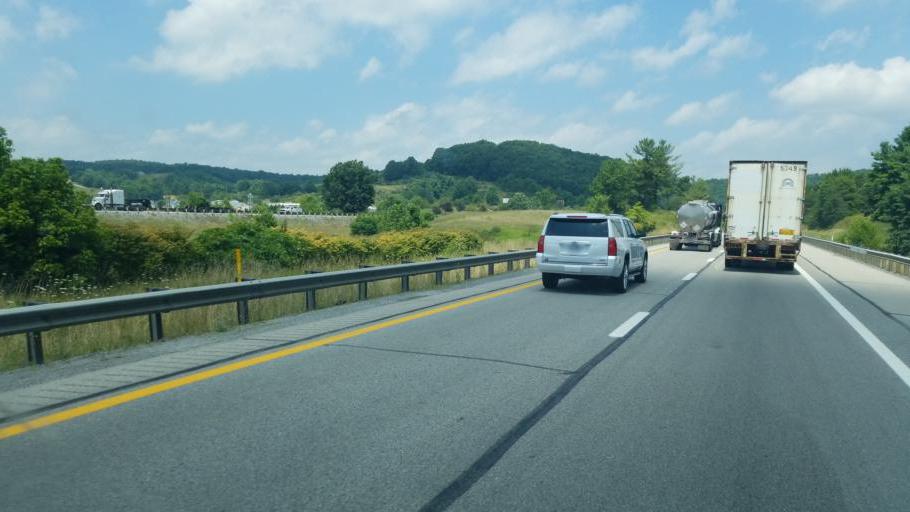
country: US
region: West Virginia
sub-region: Mercer County
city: Athens
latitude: 37.4321
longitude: -81.0655
